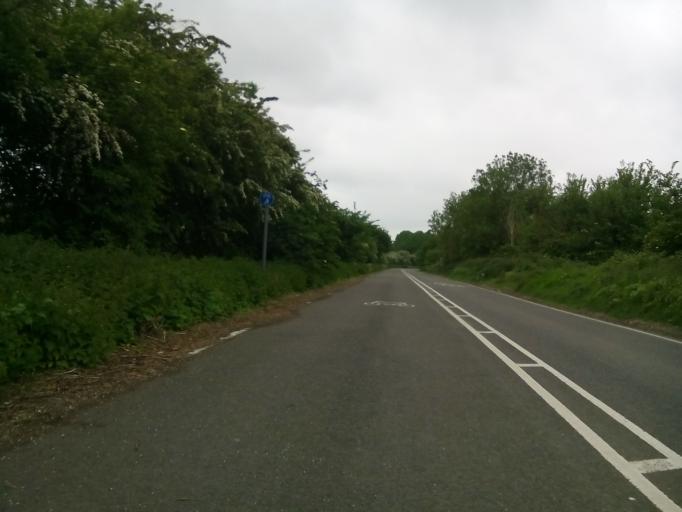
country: GB
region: England
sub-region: Cambridgeshire
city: Godmanchester
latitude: 52.3377
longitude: -0.1479
